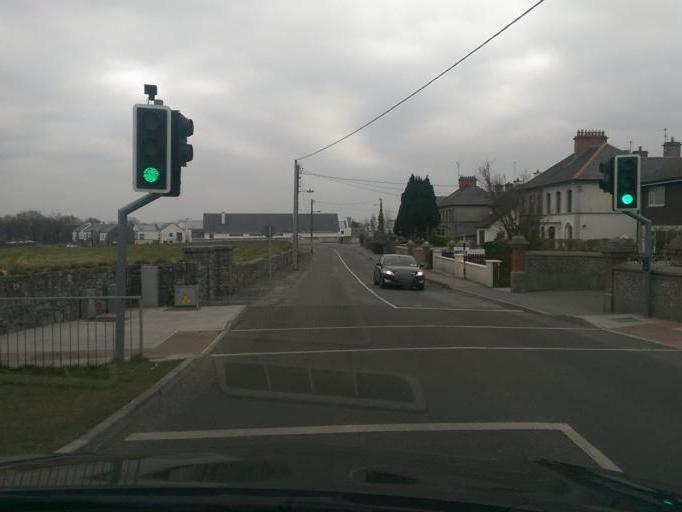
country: IE
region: Connaught
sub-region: County Galway
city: Athenry
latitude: 53.2956
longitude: -8.7519
